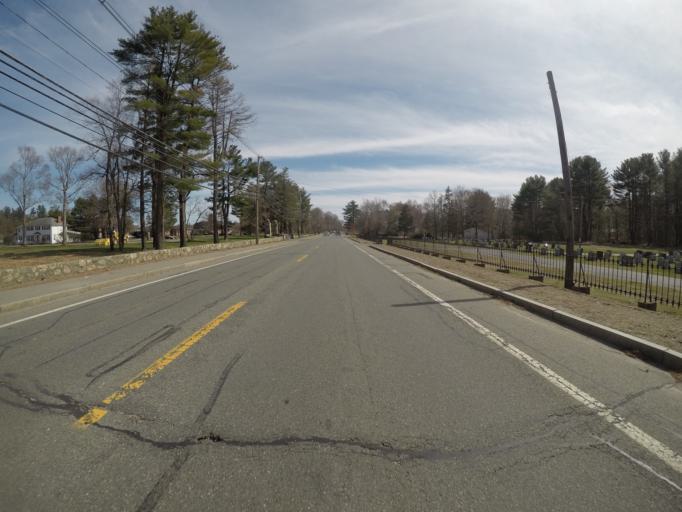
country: US
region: Massachusetts
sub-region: Bristol County
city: Easton
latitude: 42.0553
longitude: -71.0858
